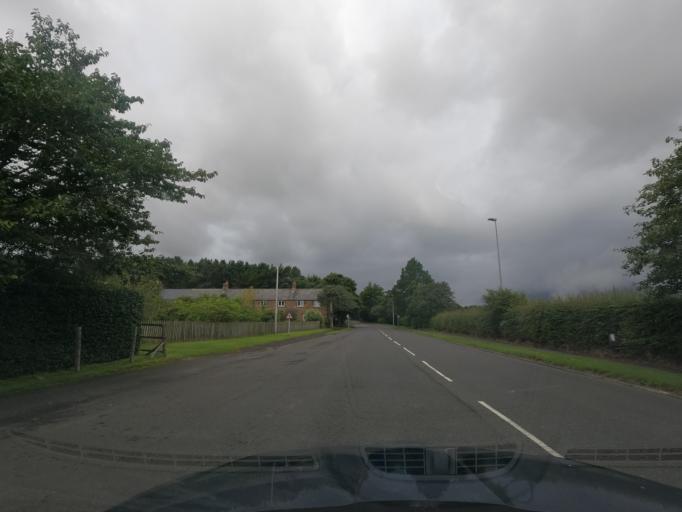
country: GB
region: England
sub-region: Northumberland
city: Ancroft
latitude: 55.7402
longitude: -1.9938
